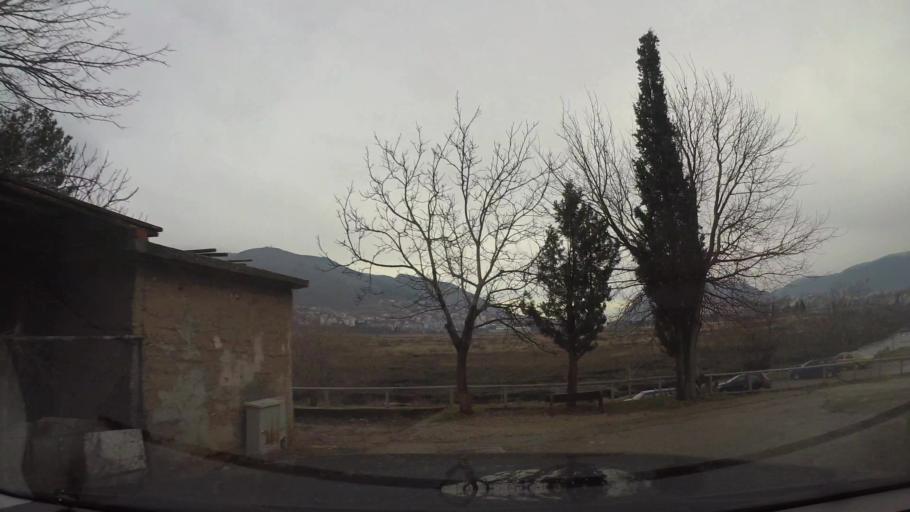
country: BA
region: Federation of Bosnia and Herzegovina
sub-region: Hercegovacko-Bosanski Kanton
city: Mostar
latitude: 43.3647
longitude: 17.8076
